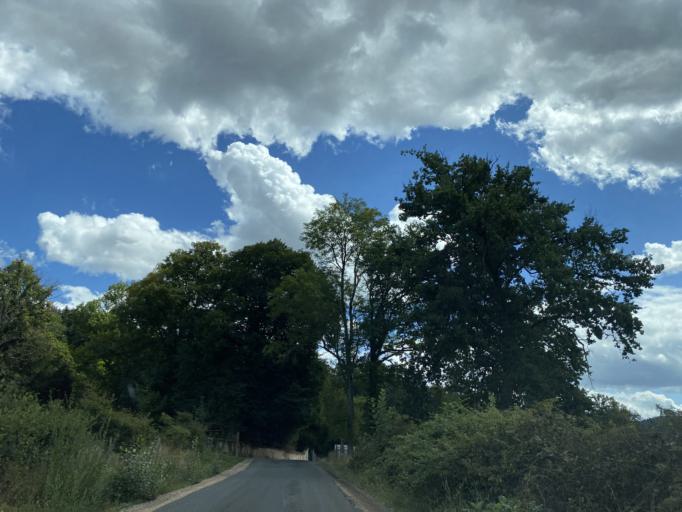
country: FR
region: Auvergne
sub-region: Departement du Puy-de-Dome
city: Courpiere
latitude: 45.7527
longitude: 3.5511
